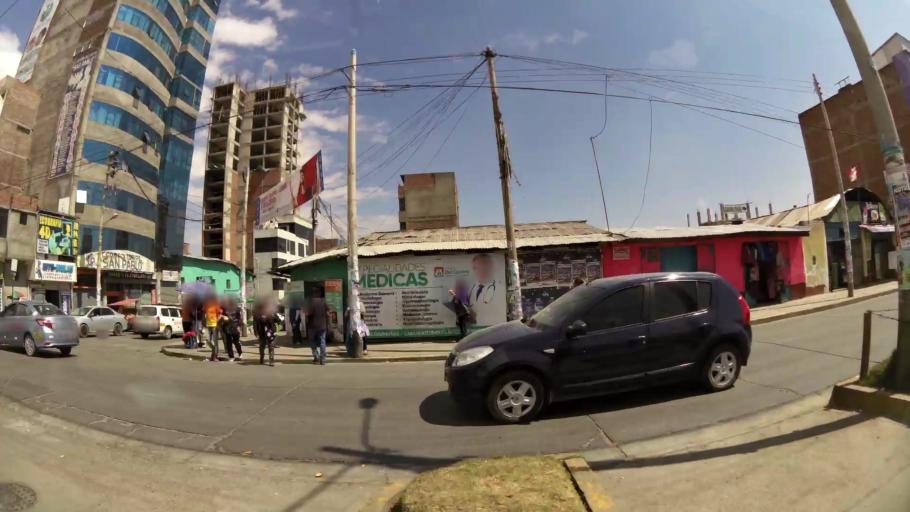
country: PE
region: Junin
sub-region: Provincia de Huancayo
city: El Tambo
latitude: -12.0699
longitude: -75.2148
